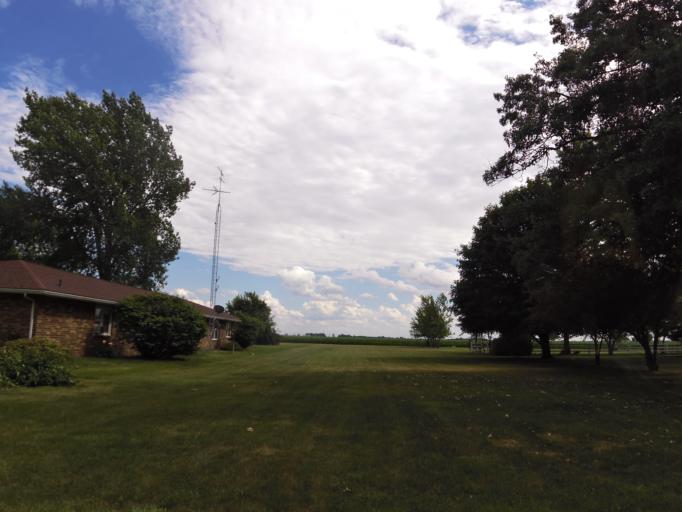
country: US
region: Iowa
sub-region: Henry County
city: Winfield
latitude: 41.1034
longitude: -91.5470
